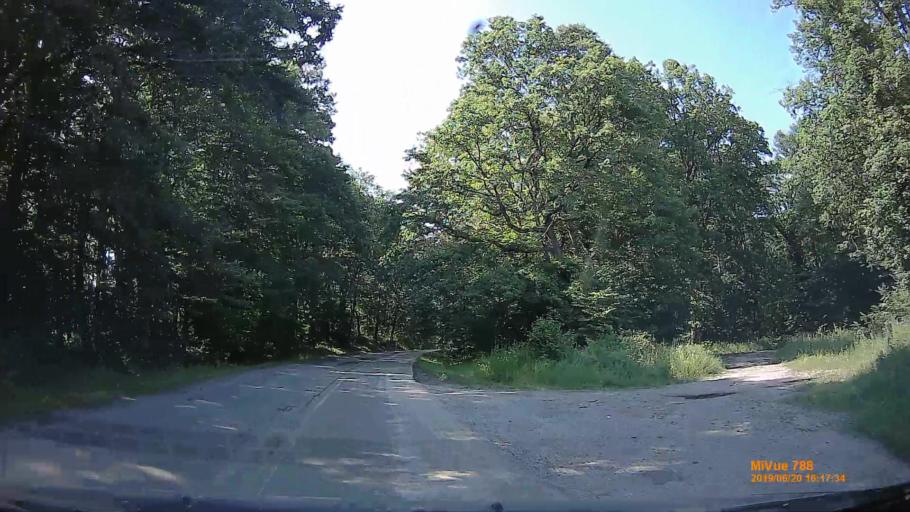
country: HU
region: Baranya
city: Buekkoesd
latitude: 46.1048
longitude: 18.0596
